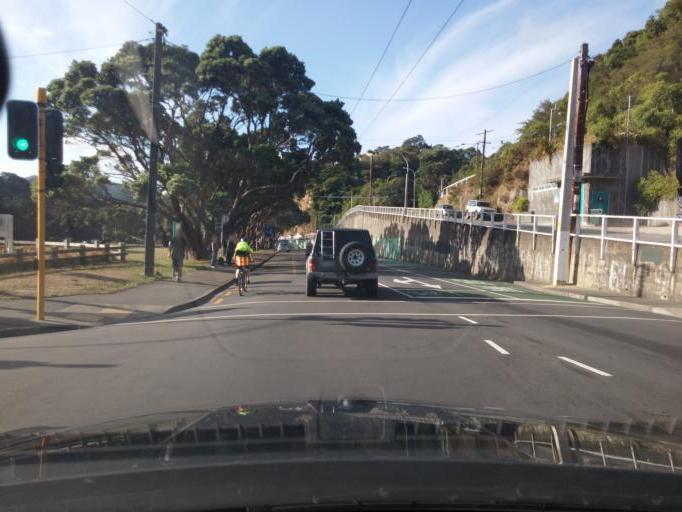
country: NZ
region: Wellington
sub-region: Wellington City
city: Kelburn
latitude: -41.2867
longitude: 174.7546
